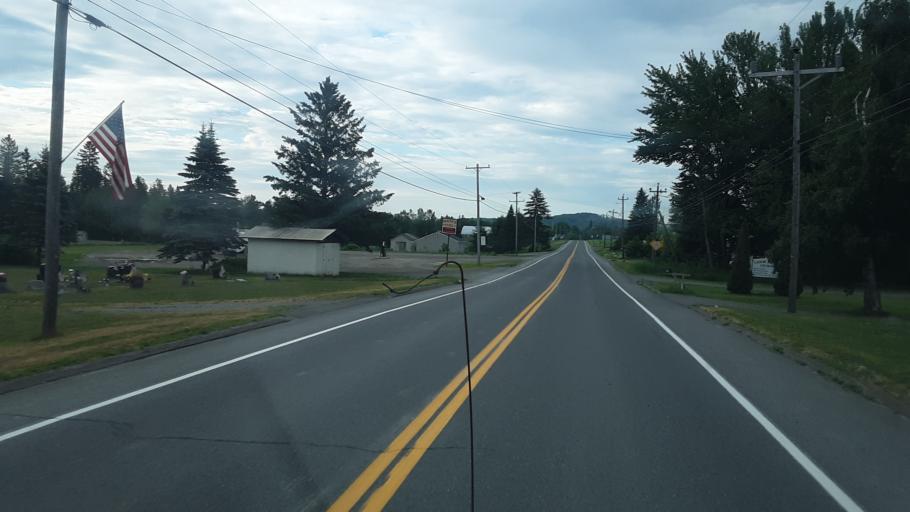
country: US
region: Maine
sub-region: Penobscot County
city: Patten
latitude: 45.9111
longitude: -68.4372
